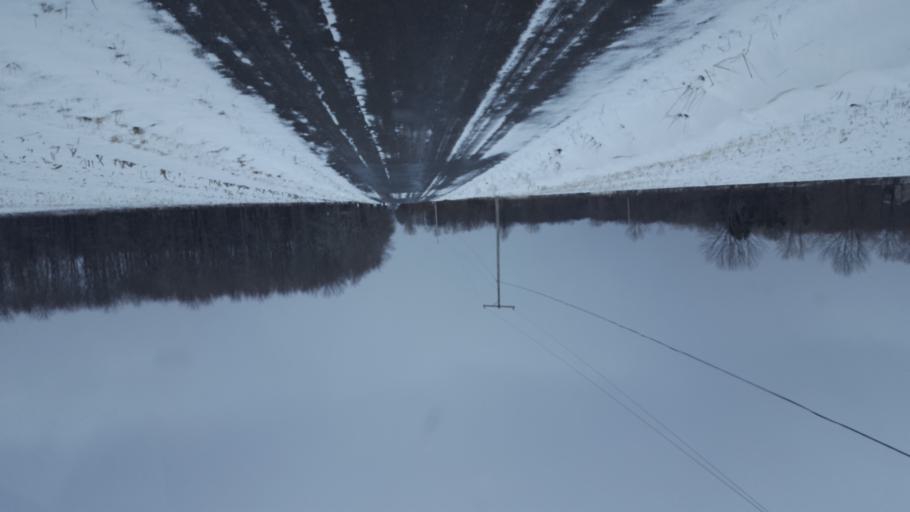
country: US
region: Pennsylvania
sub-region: Mercer County
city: Stoneboro
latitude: 41.4123
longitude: -80.0956
